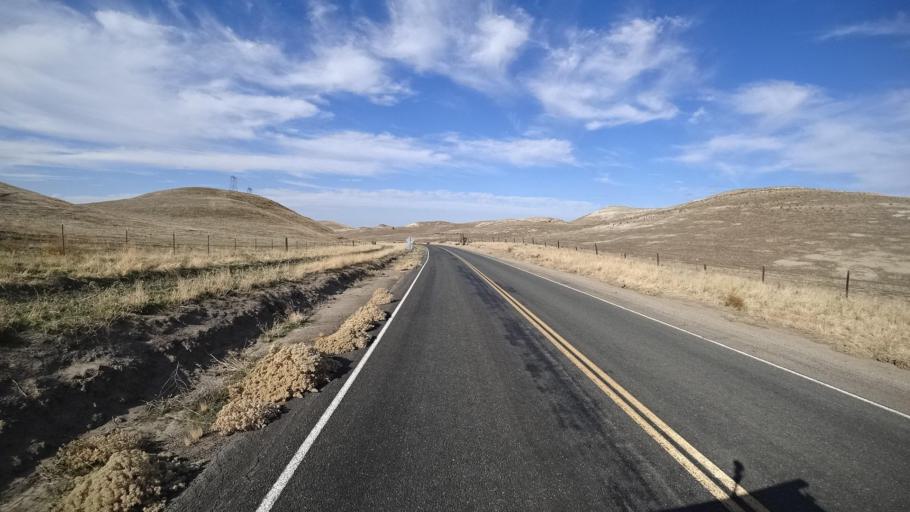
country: US
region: California
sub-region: Kern County
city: Oildale
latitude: 35.6105
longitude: -118.9167
